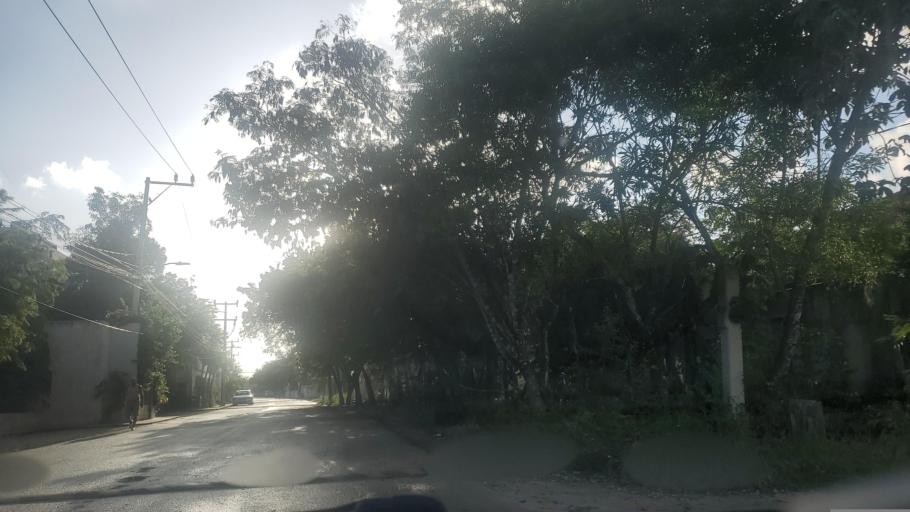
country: MX
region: Quintana Roo
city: Tulum
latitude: 20.2117
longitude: -87.4731
